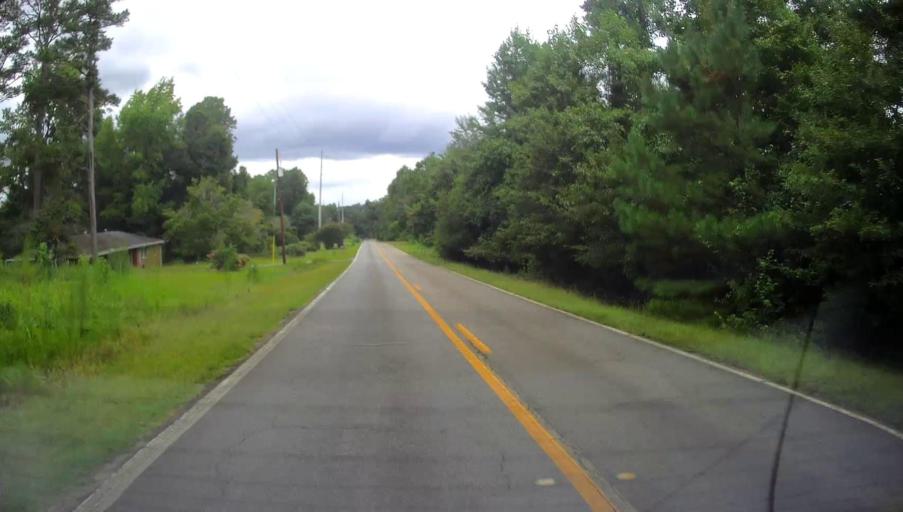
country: US
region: Georgia
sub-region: Bibb County
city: Macon
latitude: 32.7979
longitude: -83.5280
